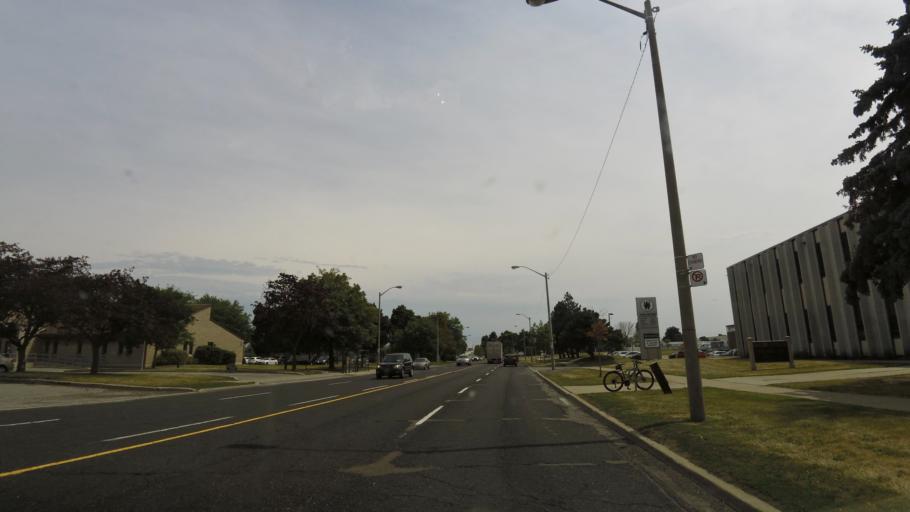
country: CA
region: Ontario
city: Etobicoke
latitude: 43.6175
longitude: -79.5108
